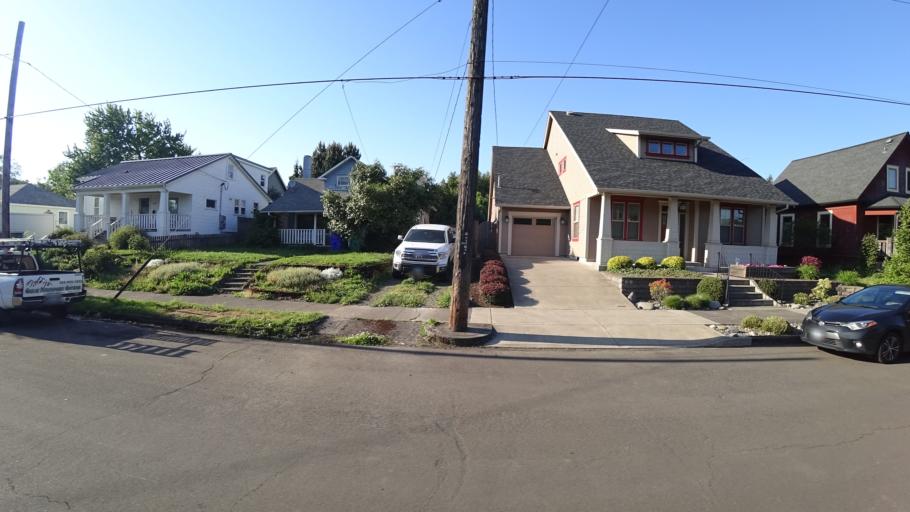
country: US
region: Oregon
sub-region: Multnomah County
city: Portland
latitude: 45.5584
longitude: -122.6879
